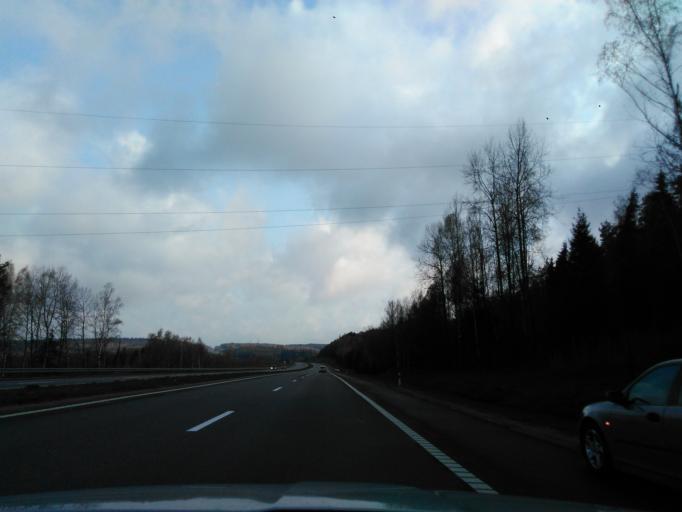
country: BY
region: Minsk
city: Lahoysk
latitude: 54.1986
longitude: 27.8168
